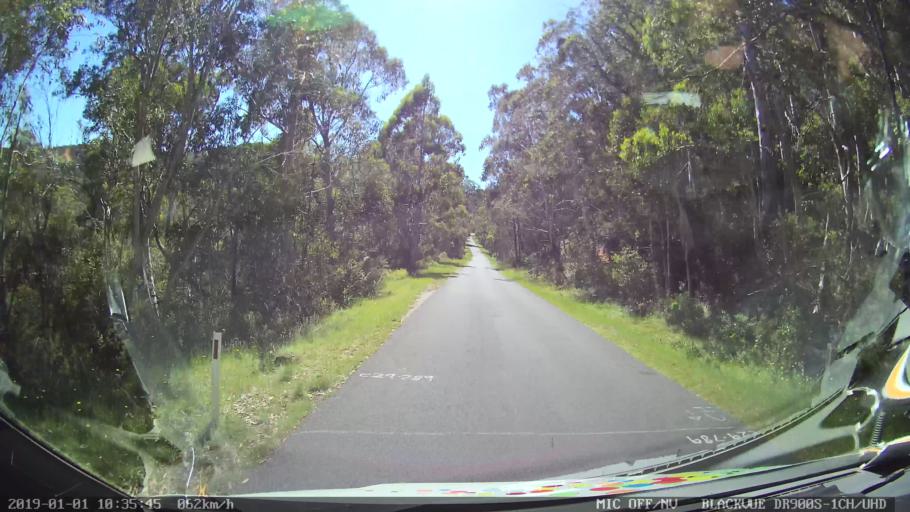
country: AU
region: New South Wales
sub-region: Snowy River
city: Jindabyne
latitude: -36.0491
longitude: 148.2909
